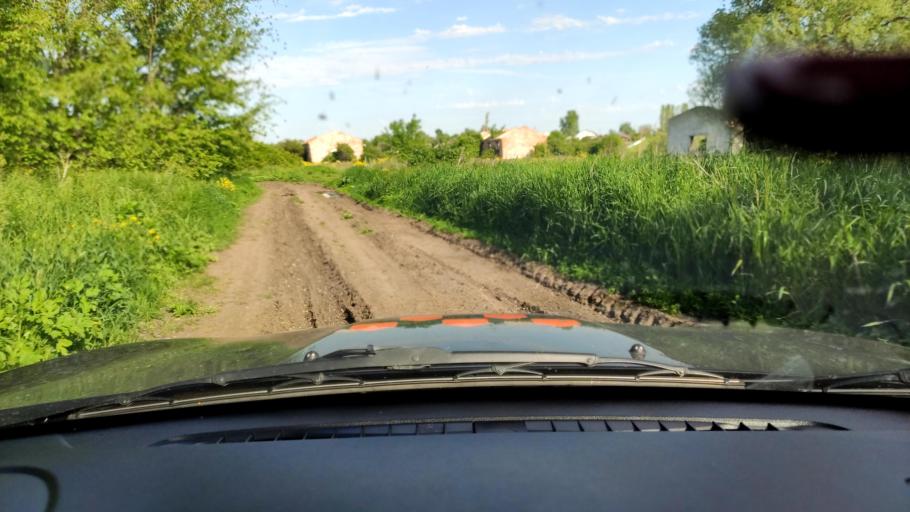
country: RU
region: Voronezj
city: Uryv-Pokrovka
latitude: 51.1200
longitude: 39.1780
